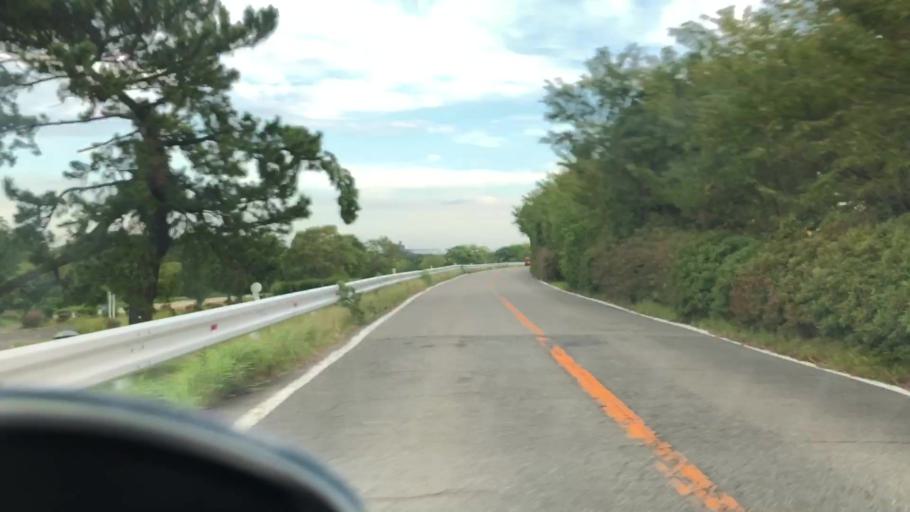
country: JP
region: Hyogo
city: Amagasaki
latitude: 34.7370
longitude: 135.3795
